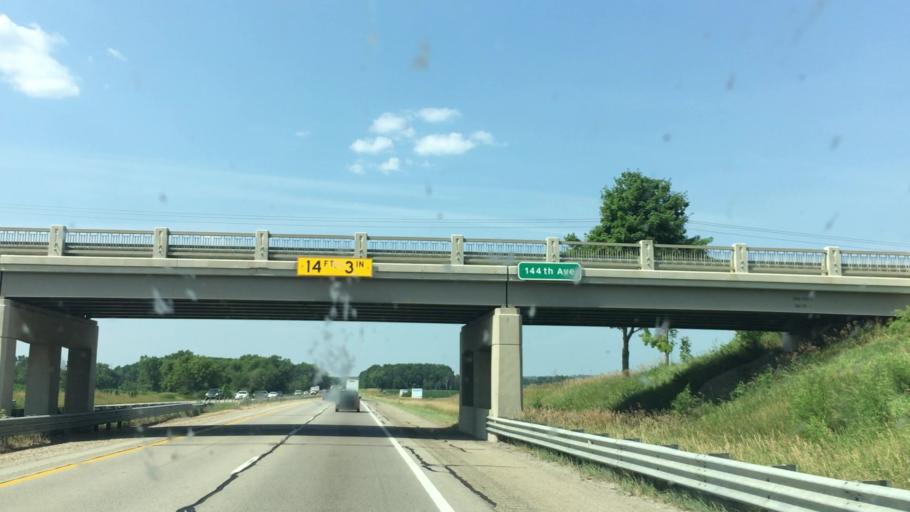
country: US
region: Michigan
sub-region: Allegan County
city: Wayland
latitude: 42.7392
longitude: -85.6732
